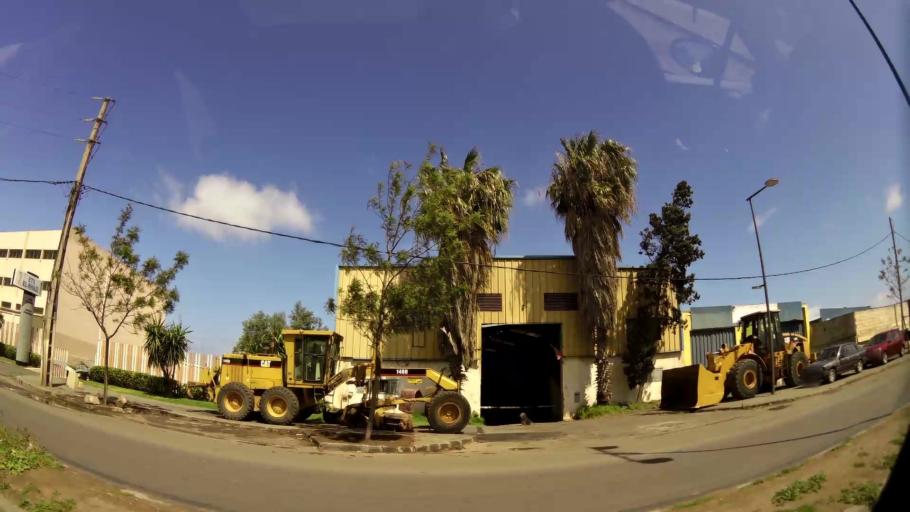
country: MA
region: Grand Casablanca
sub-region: Mediouna
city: Tit Mellil
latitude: 33.6330
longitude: -7.4687
